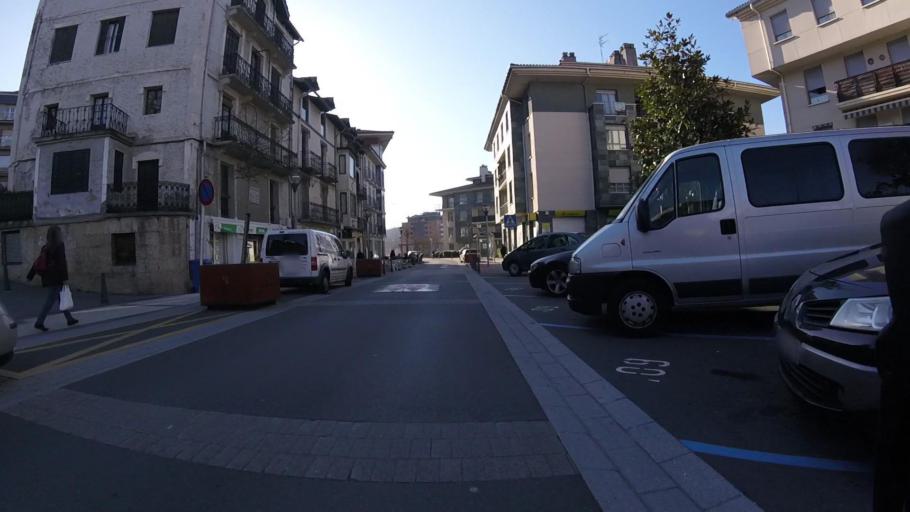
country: ES
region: Basque Country
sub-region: Provincia de Guipuzcoa
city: Astigarraga
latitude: 43.2804
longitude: -1.9495
